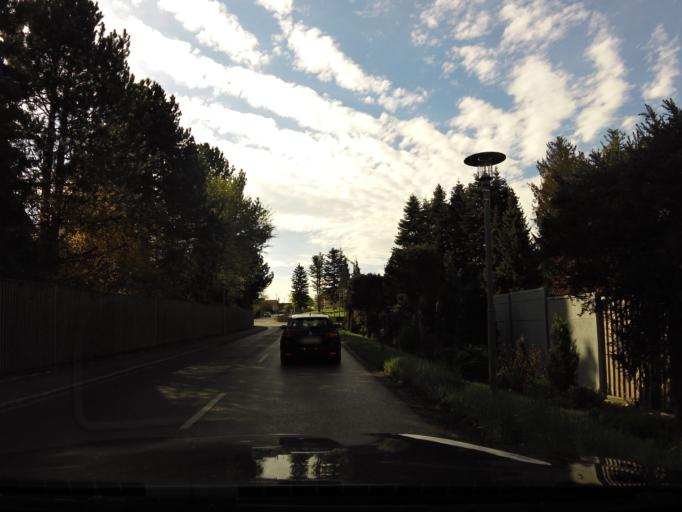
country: DE
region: Bavaria
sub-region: Upper Bavaria
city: Oberding
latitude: 48.3379
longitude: 11.8401
